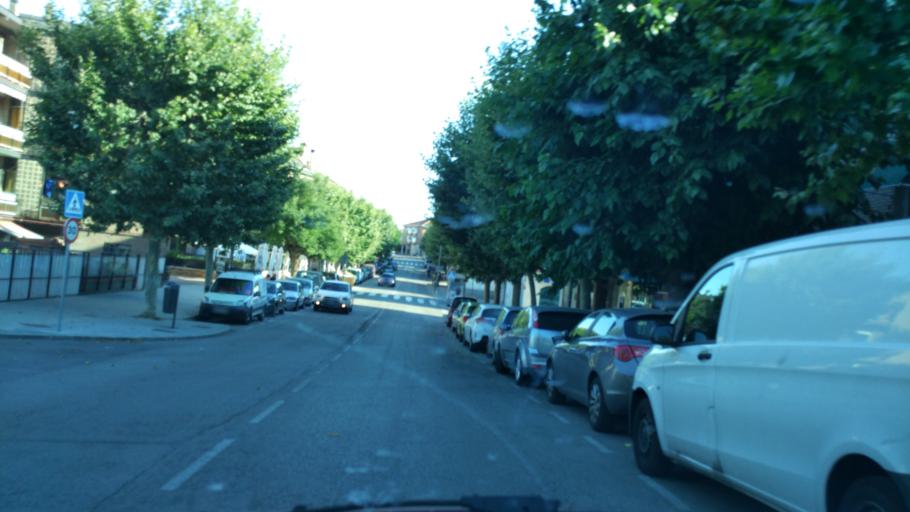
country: ES
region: Madrid
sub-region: Provincia de Madrid
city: San Agustin de Guadalix
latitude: 40.6802
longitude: -3.6142
